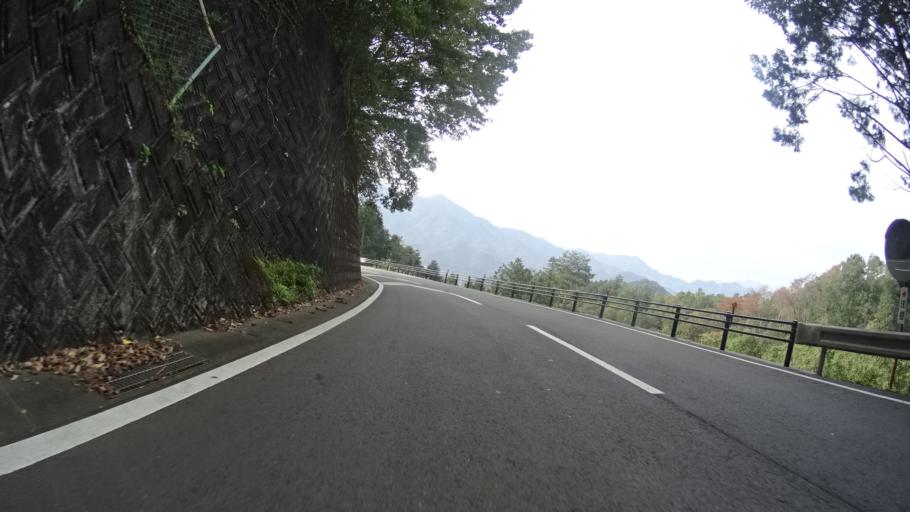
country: JP
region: Yamanashi
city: Otsuki
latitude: 35.6194
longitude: 139.0186
